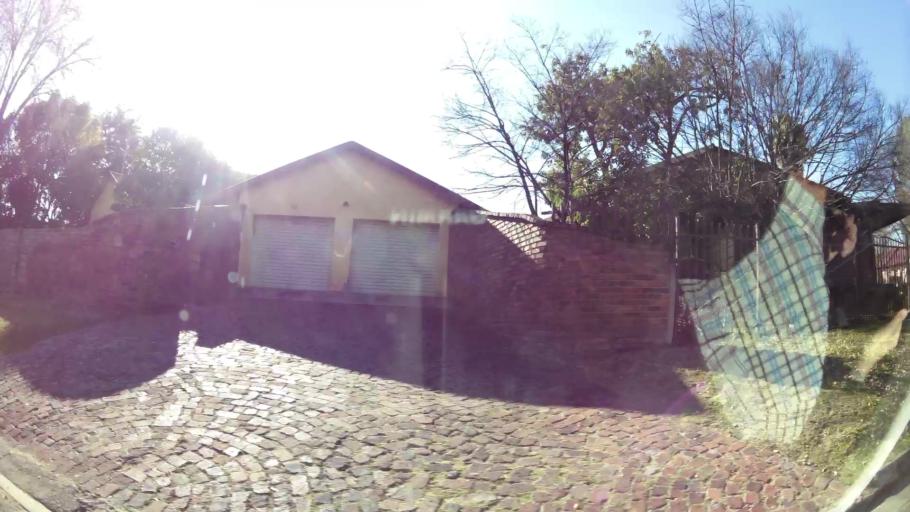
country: ZA
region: Gauteng
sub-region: City of Johannesburg Metropolitan Municipality
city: Modderfontein
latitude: -26.0577
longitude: 28.1969
